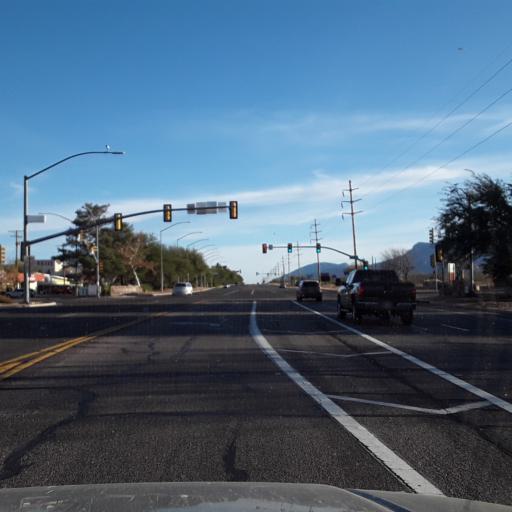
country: US
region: Arizona
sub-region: Cochise County
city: Sierra Vista
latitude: 31.5546
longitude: -110.3069
